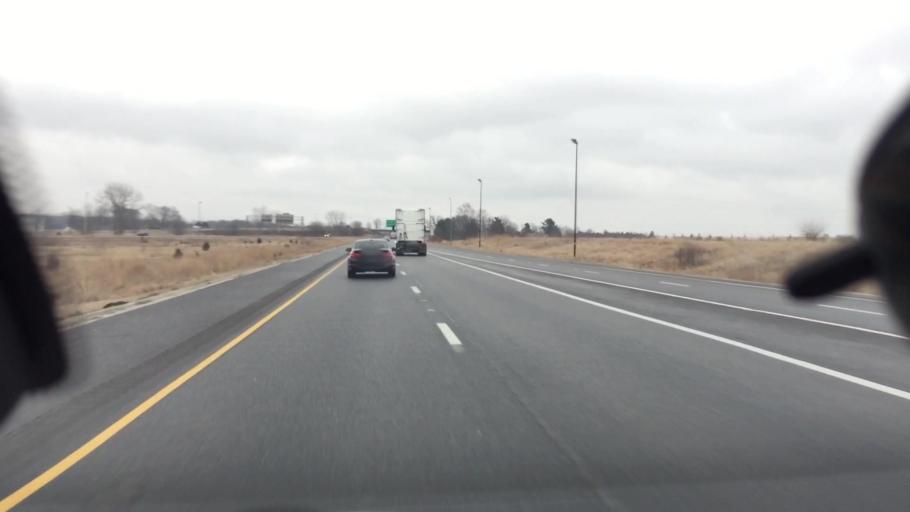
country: US
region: Illinois
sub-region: Tazewell County
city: Morton
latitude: 40.6312
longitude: -89.5161
